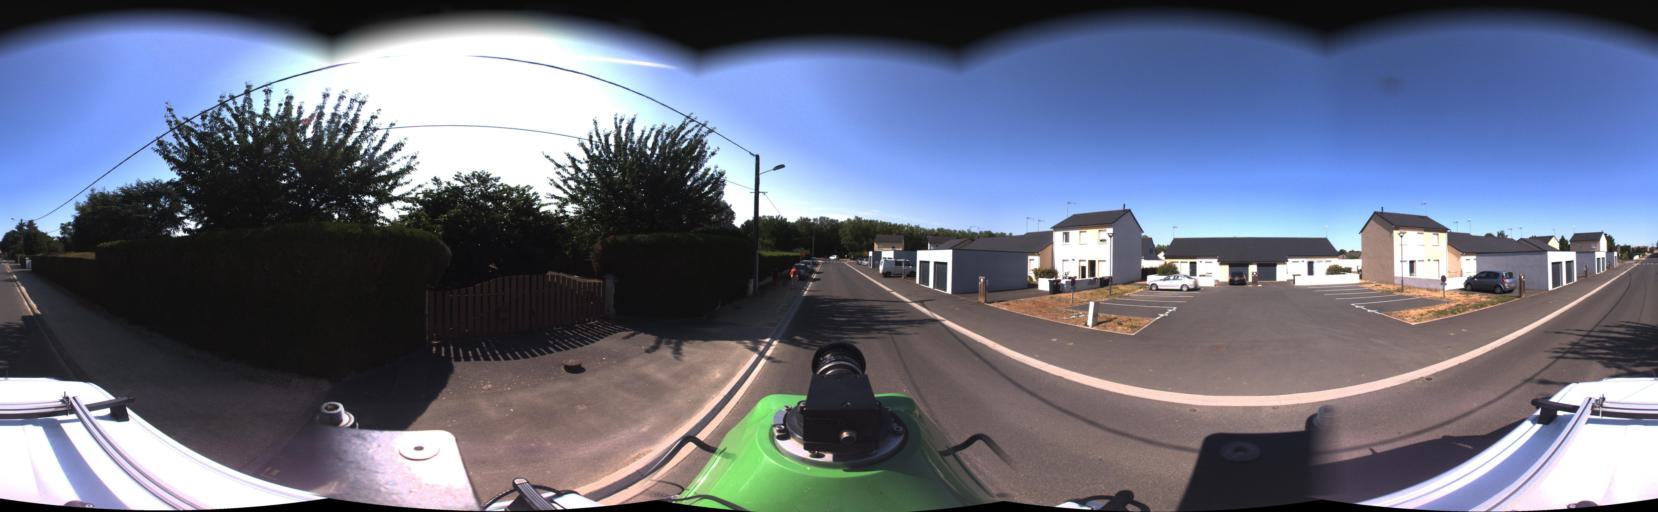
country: FR
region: Pays de la Loire
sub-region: Departement de Maine-et-Loire
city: Doue-la-Fontaine
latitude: 47.1922
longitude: -0.2974
